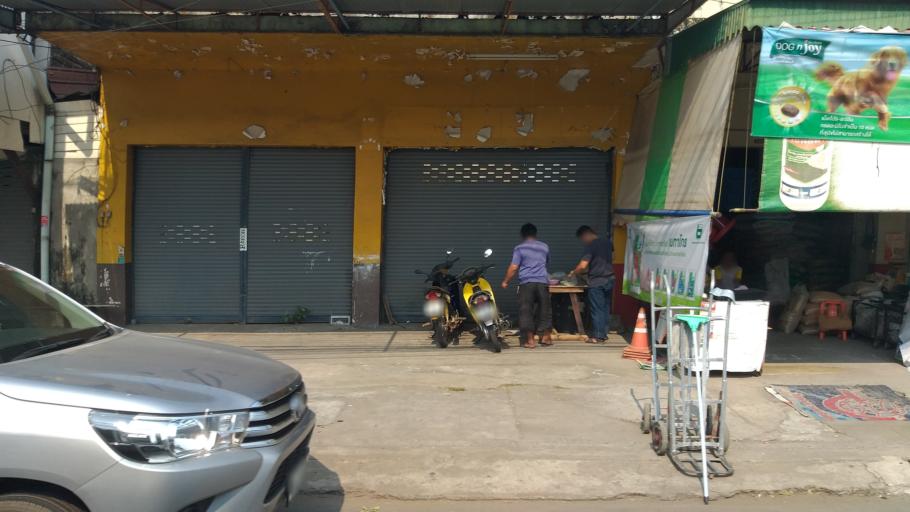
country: TH
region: Changwat Udon Thani
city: Udon Thani
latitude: 17.4022
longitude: 102.7981
